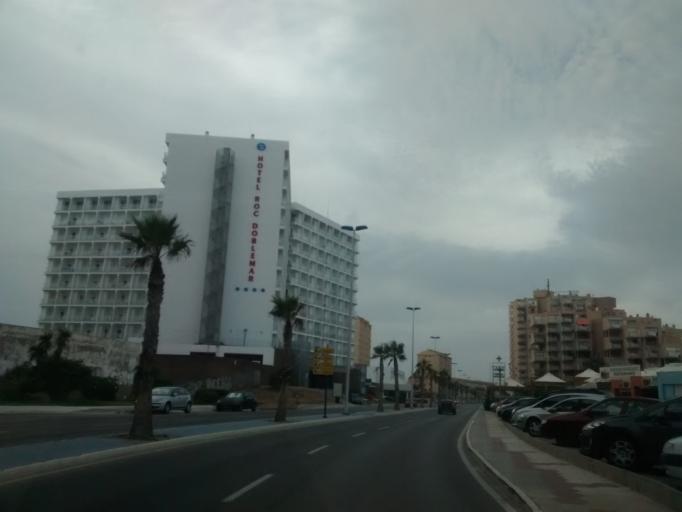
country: ES
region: Murcia
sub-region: Murcia
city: La Manga del Mar Menor
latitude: 37.6956
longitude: -0.7394
